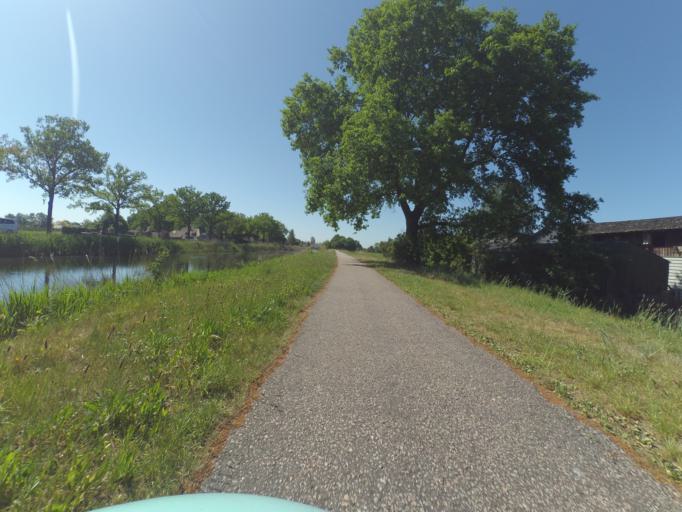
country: NL
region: Gelderland
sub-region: Gemeente Epe
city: Vaassen
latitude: 52.2578
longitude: 5.9826
